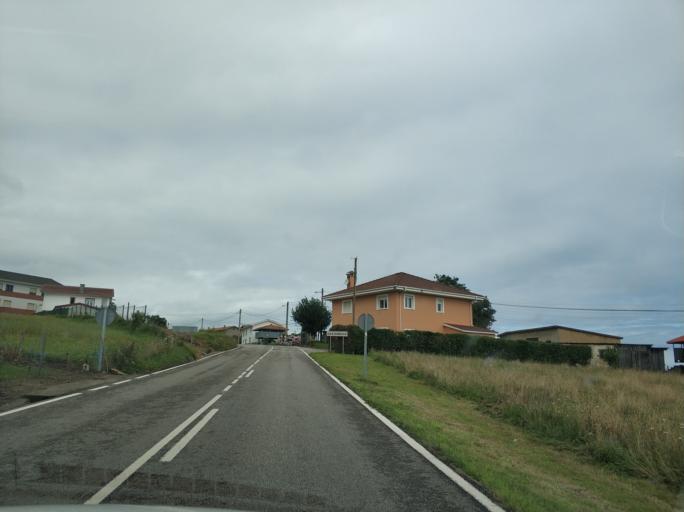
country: ES
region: Asturias
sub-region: Province of Asturias
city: Cudillero
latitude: 43.5610
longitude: -6.2939
